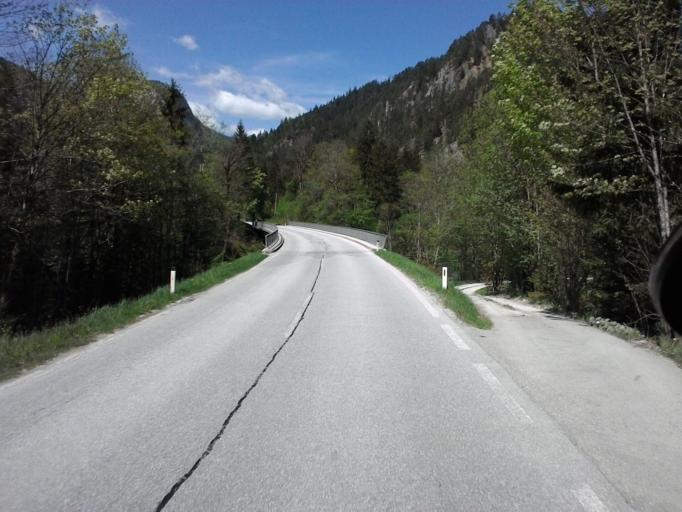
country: AT
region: Styria
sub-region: Politischer Bezirk Liezen
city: Wildalpen
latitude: 47.6744
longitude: 14.9615
